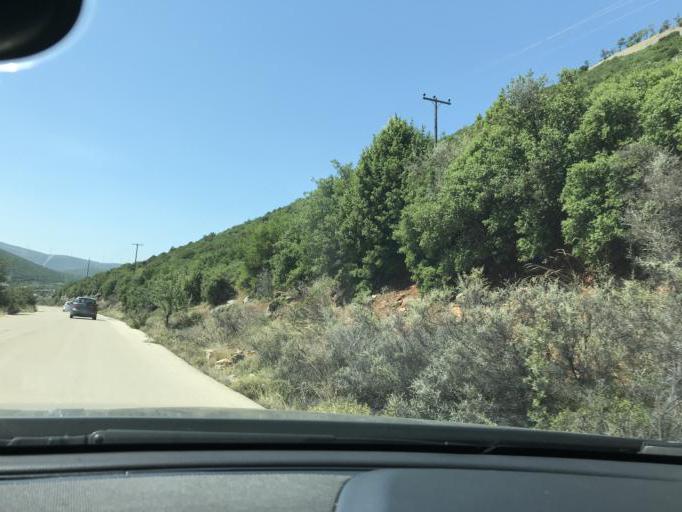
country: GR
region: Central Greece
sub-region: Nomos Voiotias
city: Distomo
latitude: 38.4714
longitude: 22.6819
